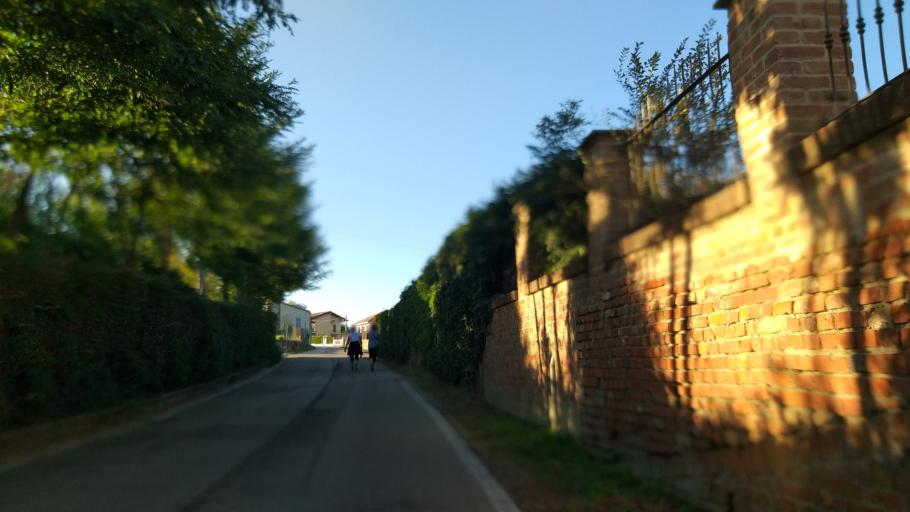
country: IT
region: Piedmont
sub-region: Provincia di Asti
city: Asti
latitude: 44.9216
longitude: 8.1997
